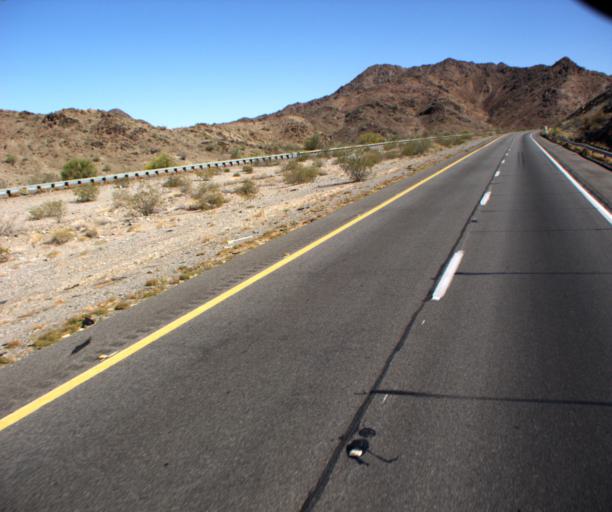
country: US
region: Arizona
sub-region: La Paz County
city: Ehrenberg
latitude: 33.6400
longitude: -114.3852
